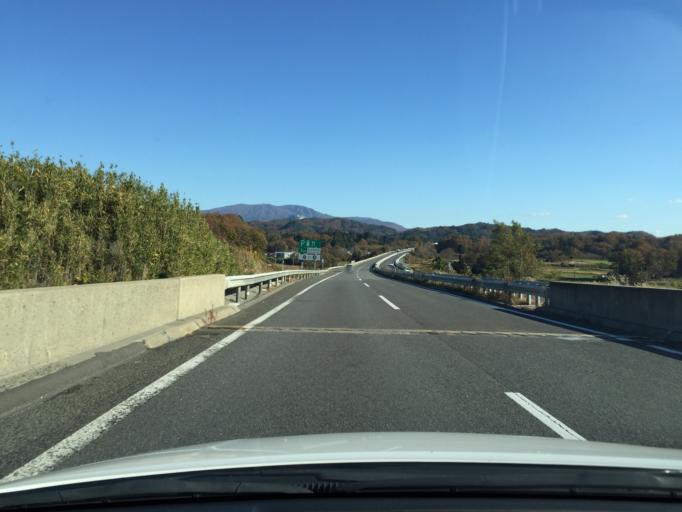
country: JP
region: Fukushima
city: Funehikimachi-funehiki
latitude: 37.3959
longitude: 140.5830
